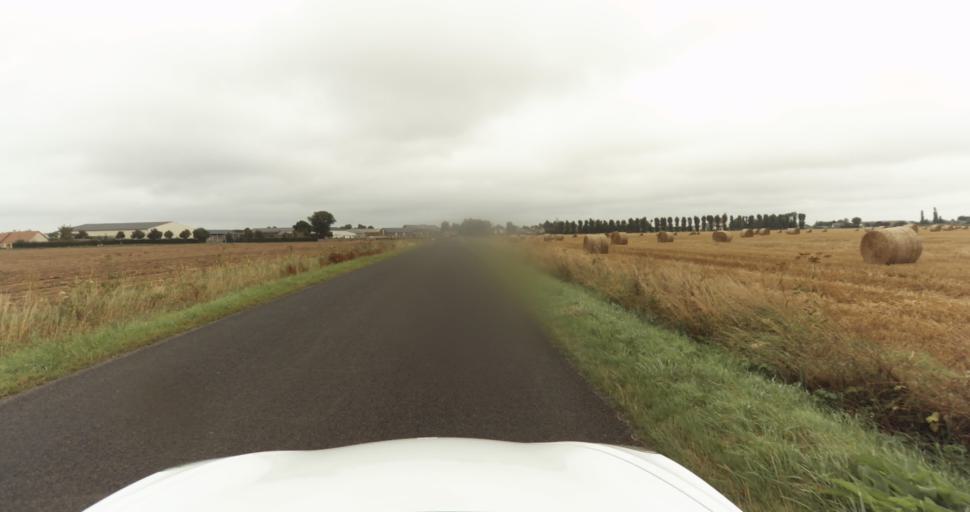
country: FR
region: Haute-Normandie
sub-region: Departement de l'Eure
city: Claville
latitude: 49.0869
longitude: 1.0666
